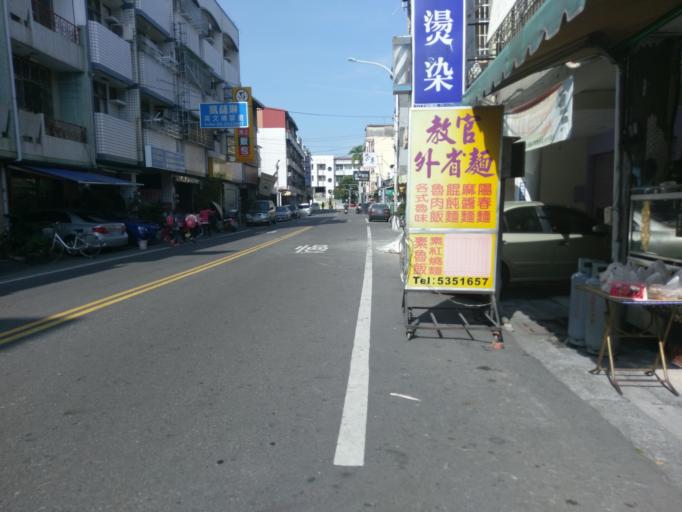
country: TW
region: Taiwan
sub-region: Yunlin
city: Douliu
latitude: 23.7105
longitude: 120.5525
